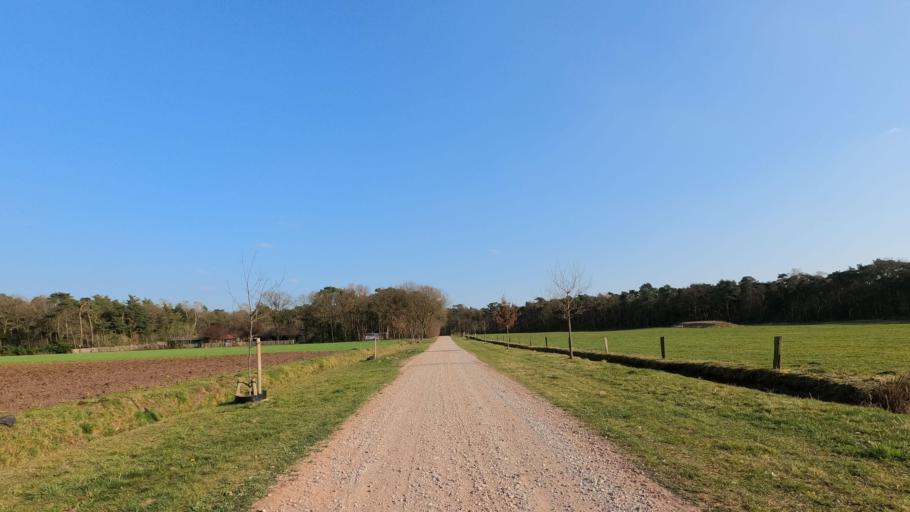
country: BE
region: Flanders
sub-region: Provincie Antwerpen
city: Baarle-Hertog
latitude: 51.3900
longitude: 4.8674
